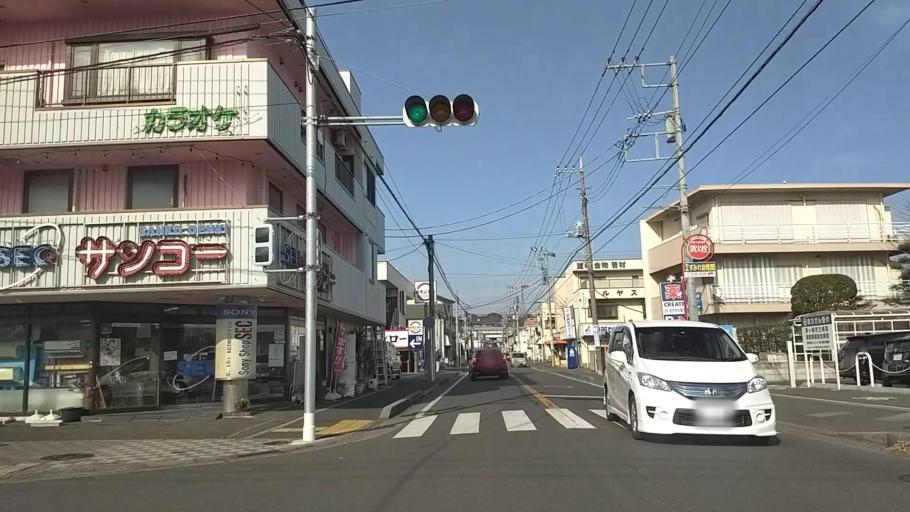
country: JP
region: Kanagawa
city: Chigasaki
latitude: 35.3469
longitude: 139.4133
